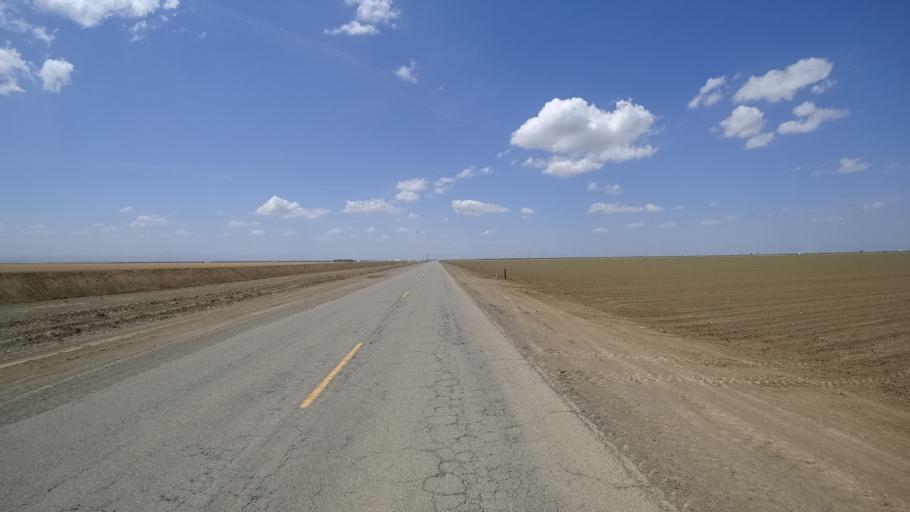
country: US
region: California
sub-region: Kings County
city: Lemoore Station
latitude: 36.1894
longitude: -119.9161
